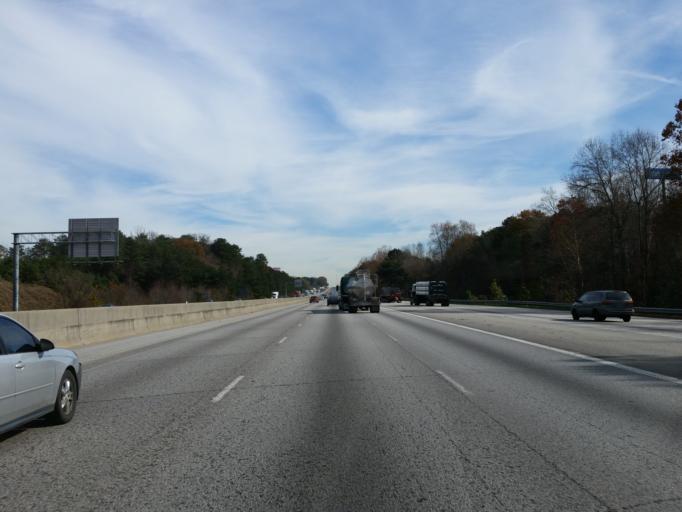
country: US
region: Georgia
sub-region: Cobb County
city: Mableton
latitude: 33.7767
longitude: -84.6038
